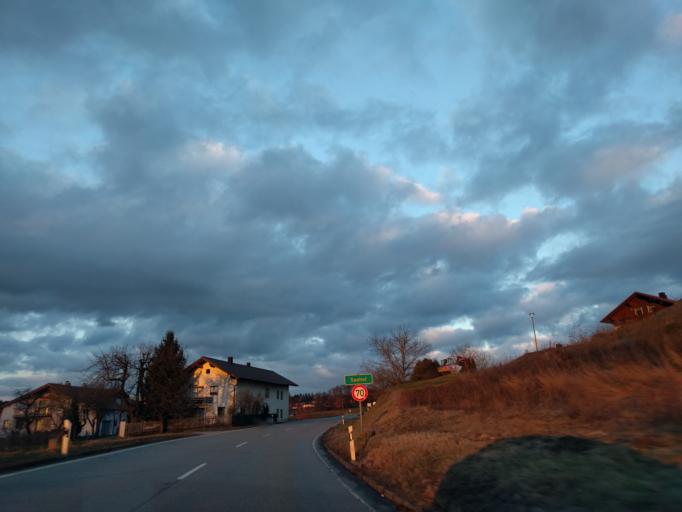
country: DE
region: Bavaria
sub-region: Lower Bavaria
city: Hofkirchen
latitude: 48.6884
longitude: 13.1184
